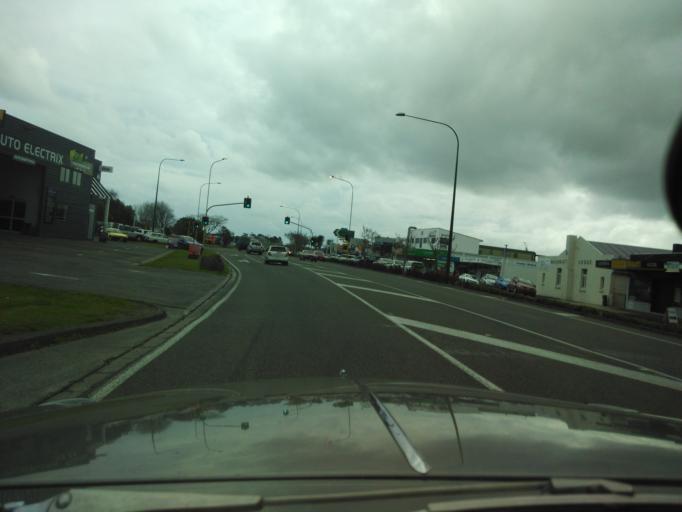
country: NZ
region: Auckland
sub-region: Auckland
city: Muriwai Beach
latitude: -36.7769
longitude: 174.5581
